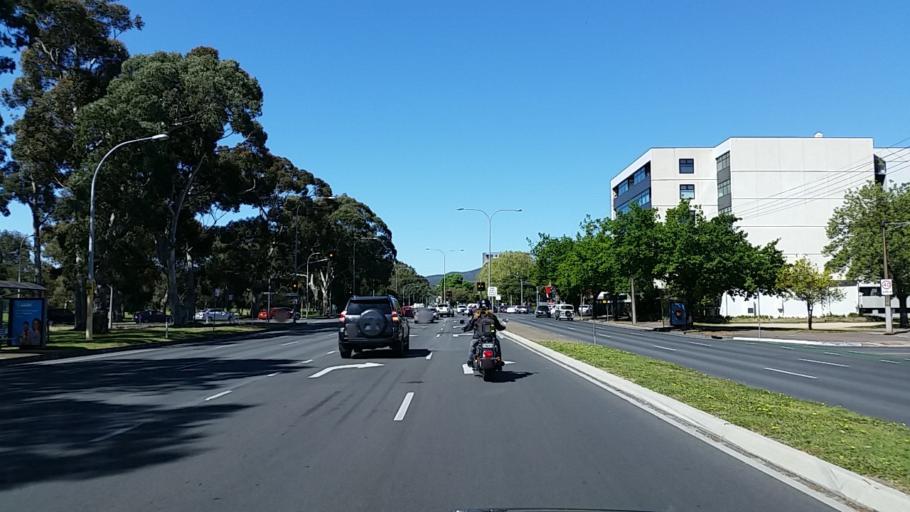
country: AU
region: South Australia
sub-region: Unley
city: Unley
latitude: -34.9405
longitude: 138.6143
